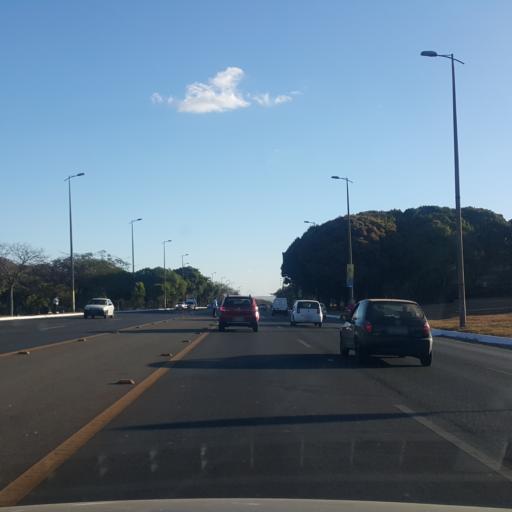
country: BR
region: Federal District
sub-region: Brasilia
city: Brasilia
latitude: -15.8150
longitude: -47.8982
